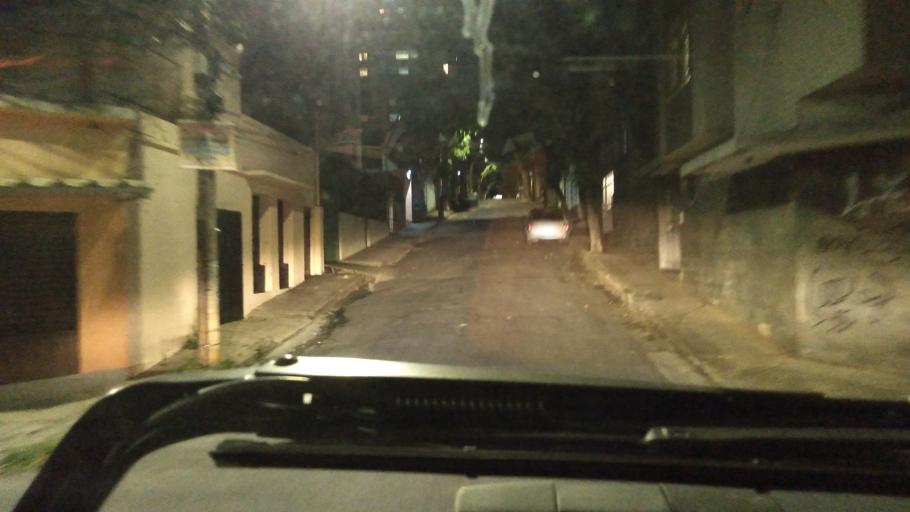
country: BR
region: Minas Gerais
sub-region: Belo Horizonte
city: Belo Horizonte
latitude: -19.9200
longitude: -43.9788
